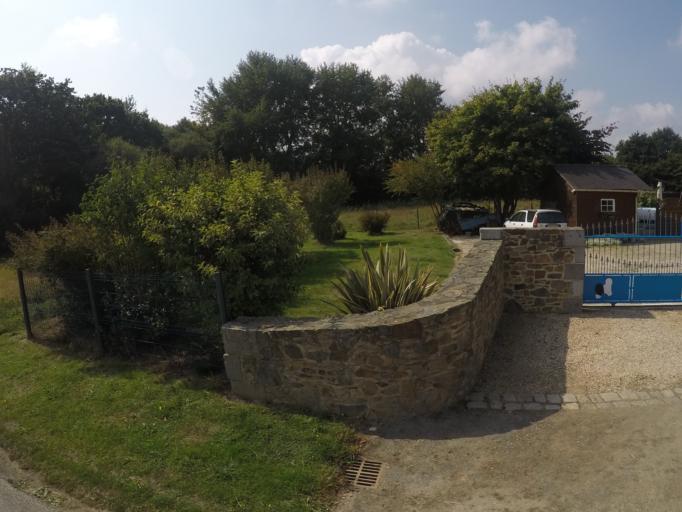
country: FR
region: Brittany
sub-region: Departement des Cotes-d'Armor
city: Tremuson
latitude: 48.5452
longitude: -2.8905
